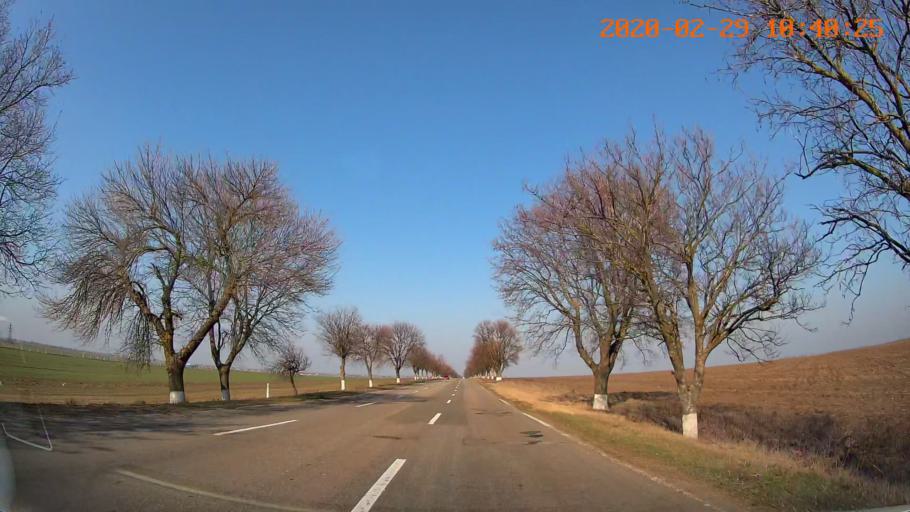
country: MD
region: Anenii Noi
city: Varnita
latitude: 47.0328
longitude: 29.4400
